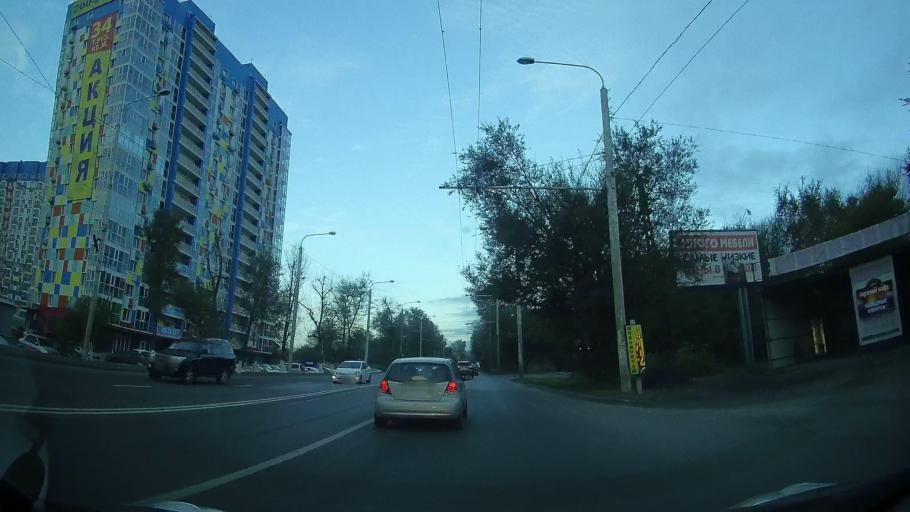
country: RU
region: Rostov
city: Severnyy
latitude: 47.2573
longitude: 39.6396
